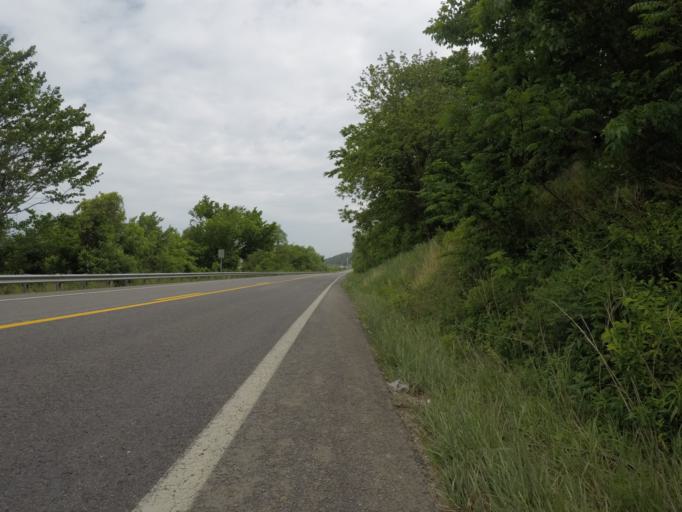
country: US
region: West Virginia
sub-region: Wayne County
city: Kenova
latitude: 38.3632
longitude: -82.5928
